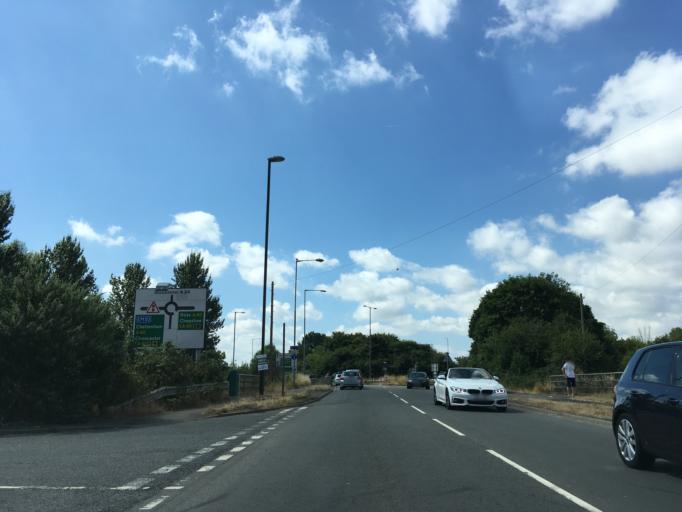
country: GB
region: England
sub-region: Gloucestershire
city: Gloucester
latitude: 51.8835
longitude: -2.2376
